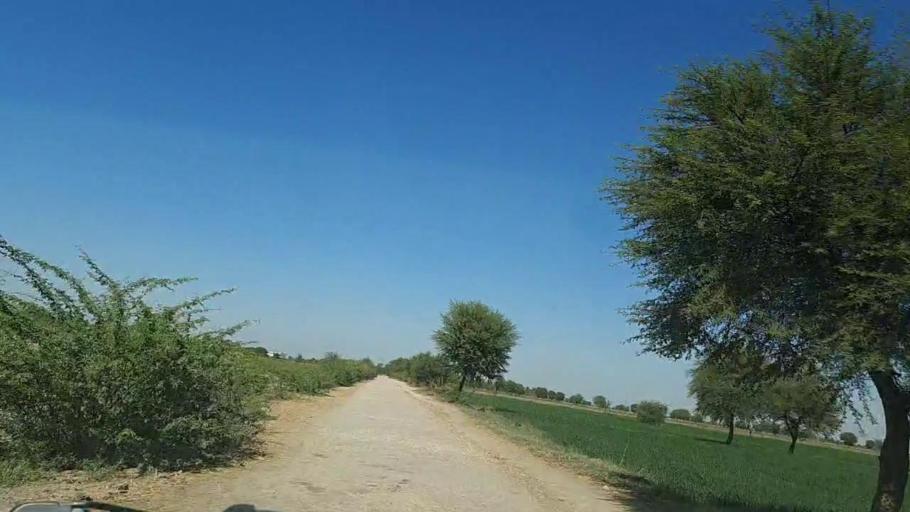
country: PK
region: Sindh
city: Dhoro Naro
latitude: 25.5224
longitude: 69.5061
